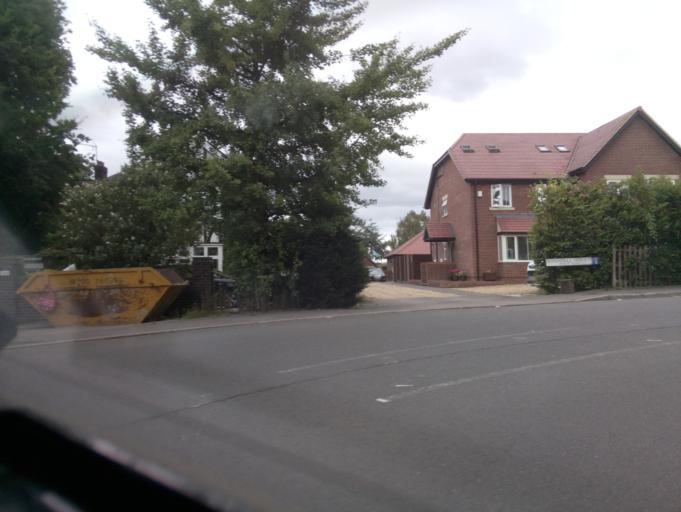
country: GB
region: England
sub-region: Gloucestershire
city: Gloucester
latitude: 51.8412
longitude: -2.2393
